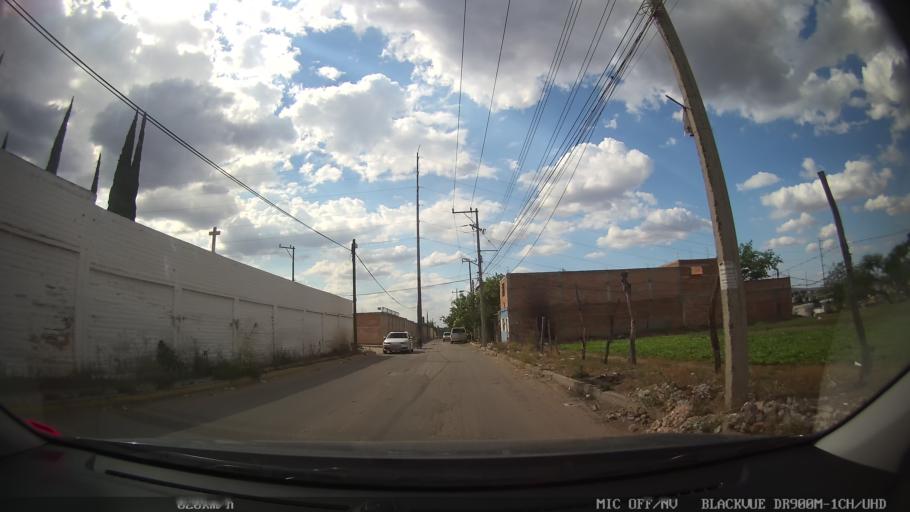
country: MX
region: Jalisco
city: Tlaquepaque
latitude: 20.6641
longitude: -103.2639
